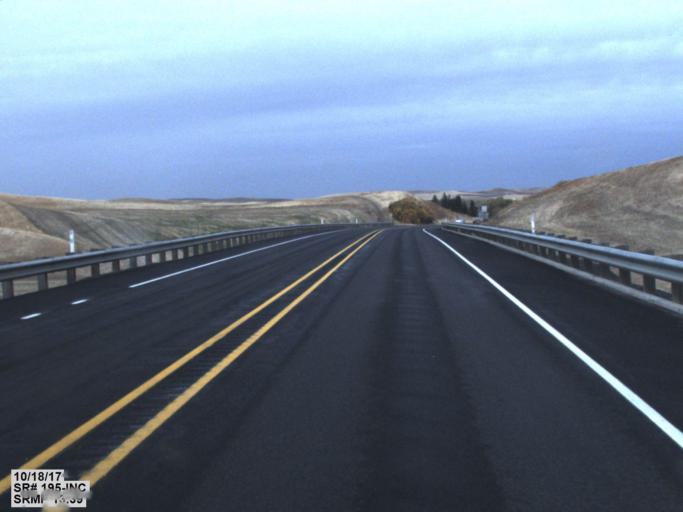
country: US
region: Washington
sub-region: Whitman County
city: Pullman
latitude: 46.6225
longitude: -117.1669
